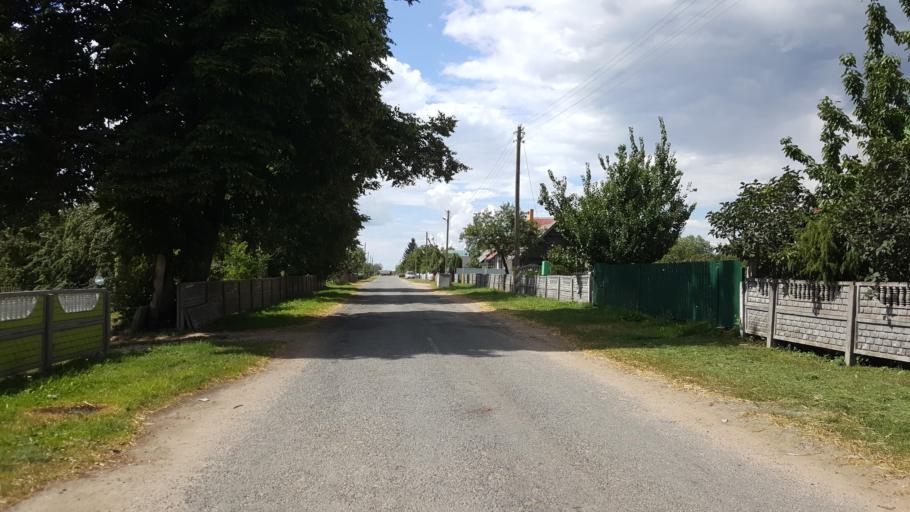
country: BY
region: Brest
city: Zhabinka
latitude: 52.2690
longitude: 23.9979
